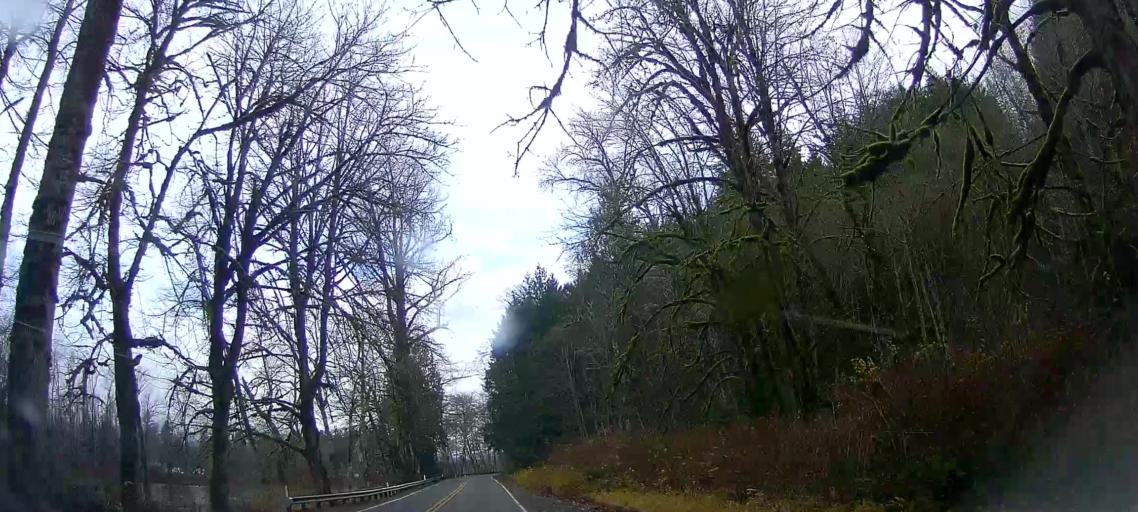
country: US
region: Washington
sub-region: Skagit County
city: Sedro-Woolley
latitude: 48.5146
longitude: -121.9814
